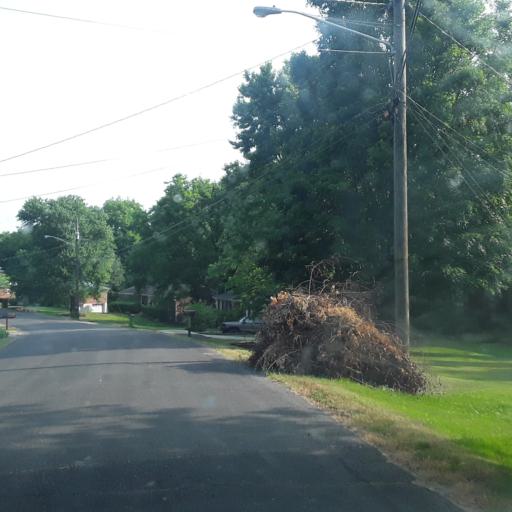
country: US
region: Tennessee
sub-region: Williamson County
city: Brentwood
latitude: 36.0599
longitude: -86.7511
